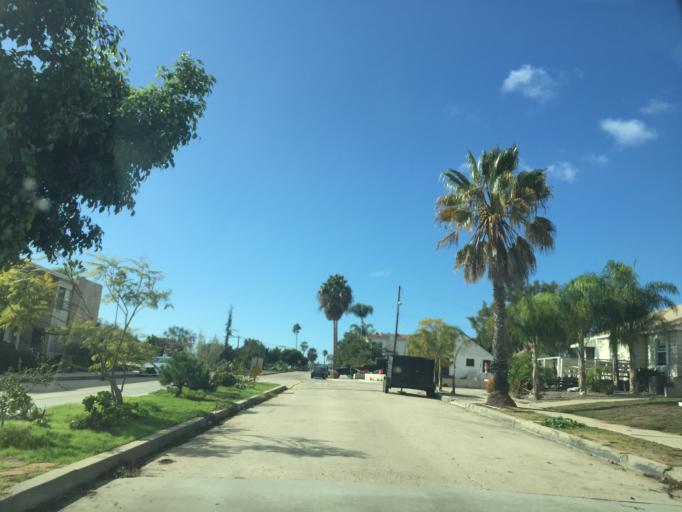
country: US
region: California
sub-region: San Diego County
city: La Jolla
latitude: 32.7952
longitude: -117.2349
